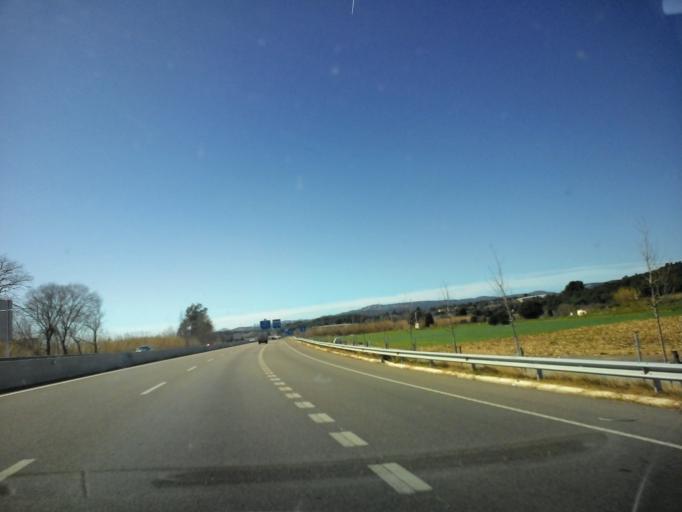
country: ES
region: Catalonia
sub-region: Provincia de Girona
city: Palamos
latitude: 41.8619
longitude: 3.1285
